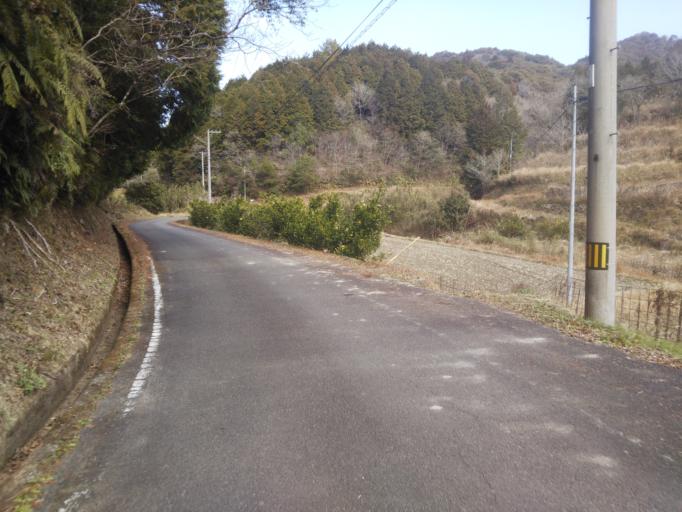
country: JP
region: Kochi
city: Nakamura
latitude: 33.0366
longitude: 132.9849
